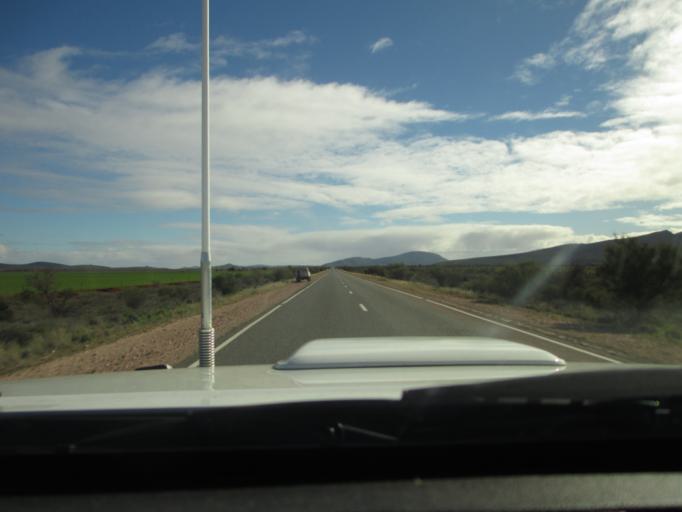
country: AU
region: South Australia
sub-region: Flinders Ranges
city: Quorn
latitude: -31.8650
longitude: 138.4052
